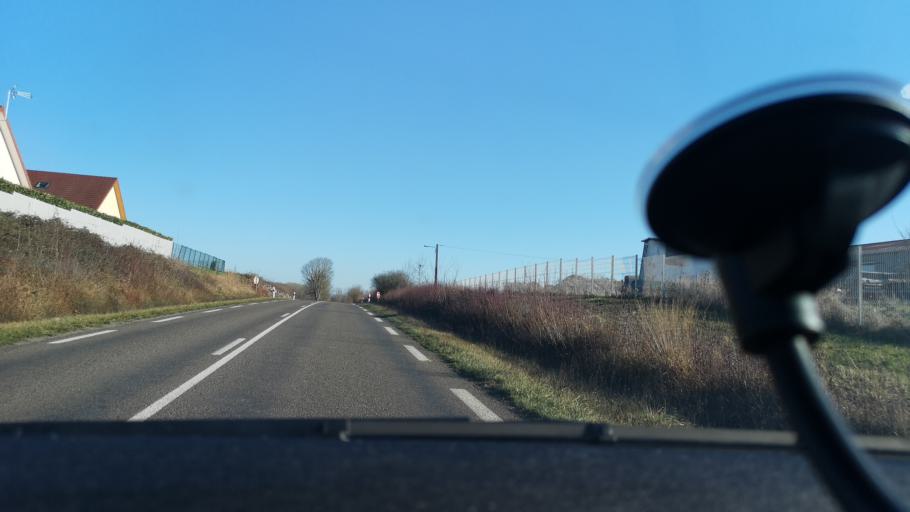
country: FR
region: Franche-Comte
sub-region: Departement du Jura
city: Bletterans
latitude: 46.7444
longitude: 5.4114
